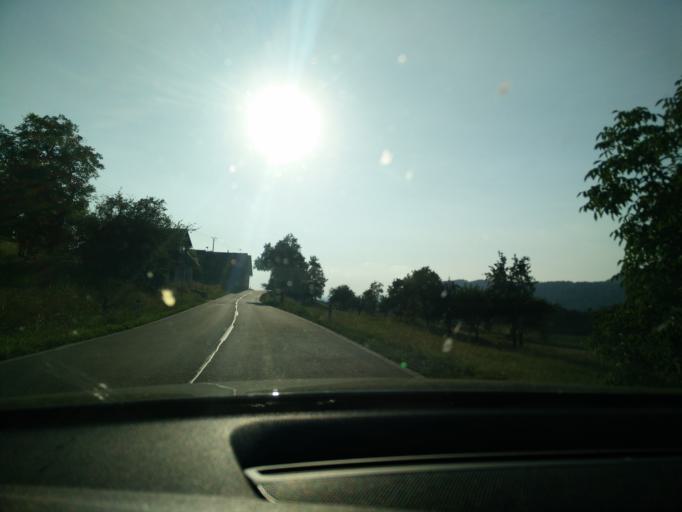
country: AT
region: Carinthia
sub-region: Politischer Bezirk Klagenfurt Land
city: Ferlach
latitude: 46.5388
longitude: 14.3506
